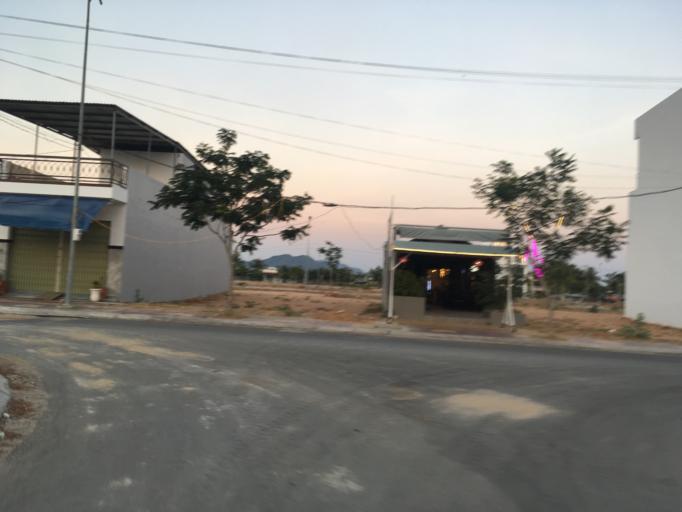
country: VN
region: Ninh Thuan
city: Phan Rang-Thap Cham
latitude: 11.5719
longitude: 108.9968
